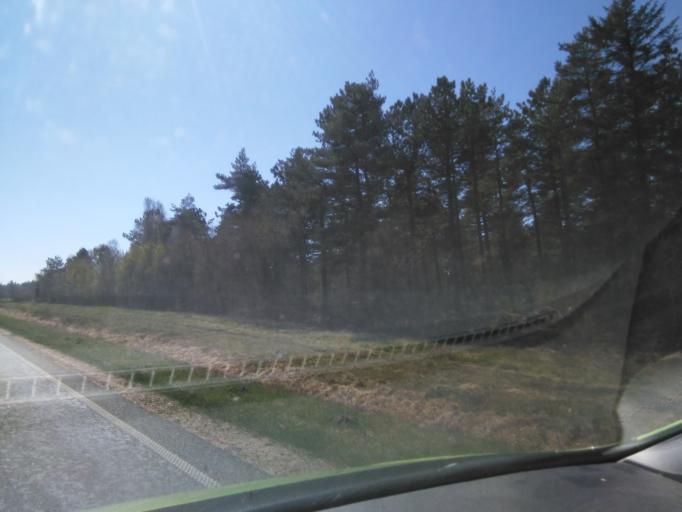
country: DK
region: South Denmark
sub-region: Varde Kommune
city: Oksbol
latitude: 55.5972
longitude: 8.2255
